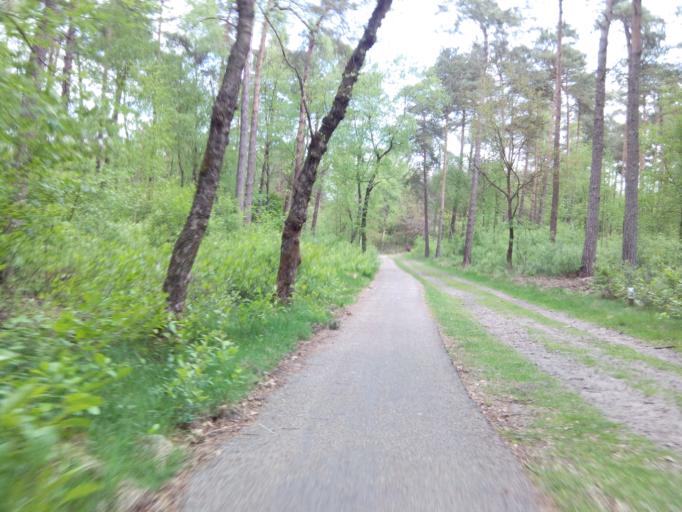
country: NL
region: Gelderland
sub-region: Gemeente Ede
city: Otterlo
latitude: 52.0822
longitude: 5.7618
